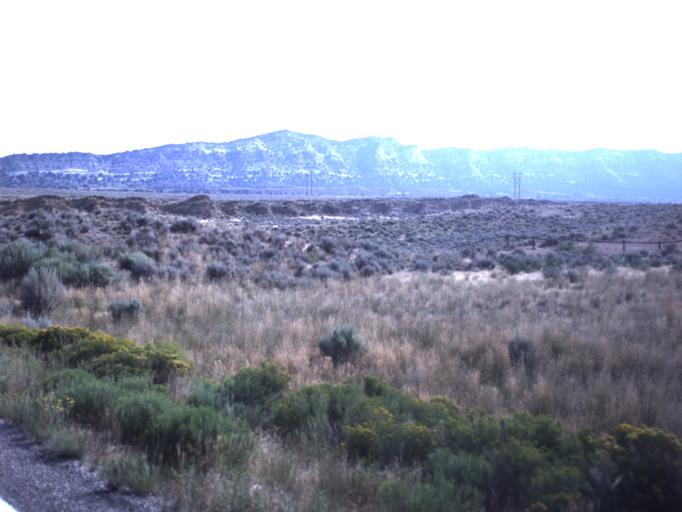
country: US
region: Utah
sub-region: Daggett County
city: Manila
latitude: 40.9886
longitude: -109.4372
